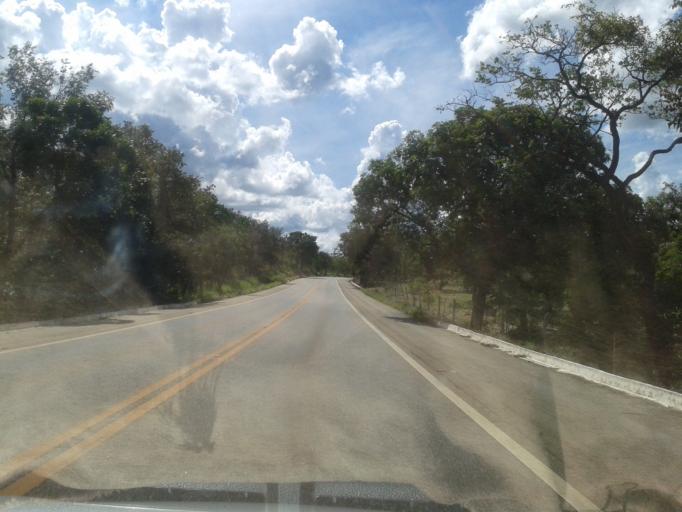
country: BR
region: Goias
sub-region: Itapuranga
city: Itapuranga
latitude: -15.4942
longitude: -50.3153
